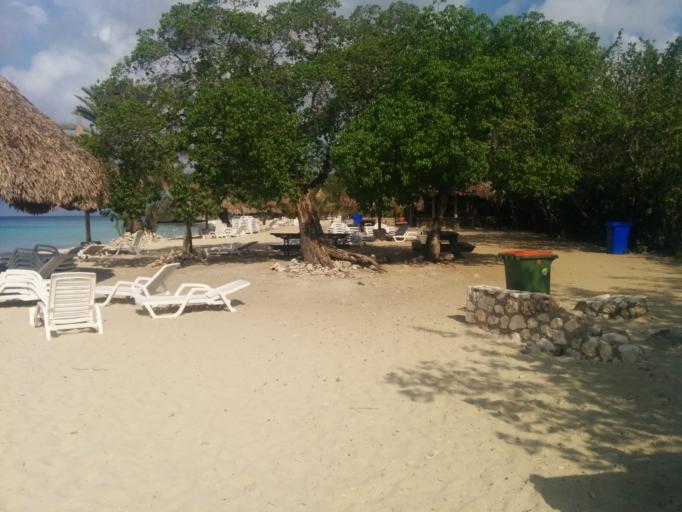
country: CW
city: Dorp Soto
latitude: 12.2276
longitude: -69.0918
